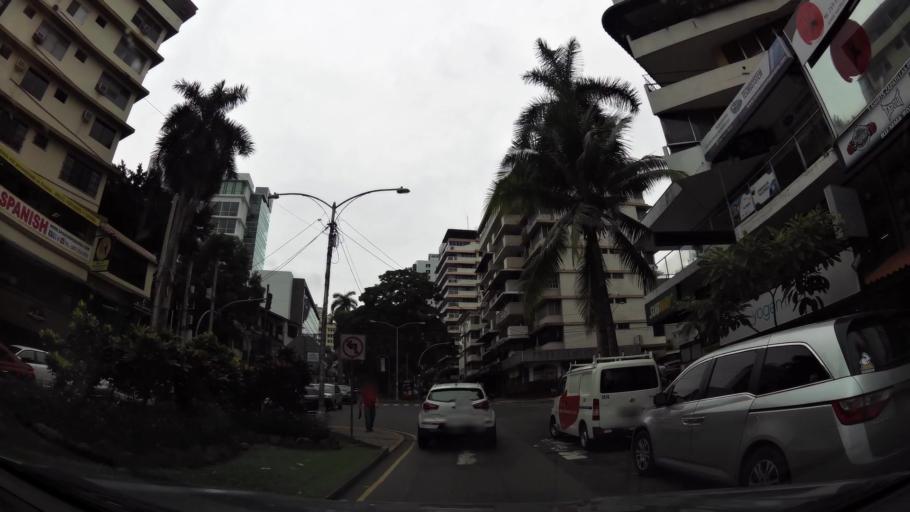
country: PA
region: Panama
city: Panama
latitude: 8.9890
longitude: -79.5277
